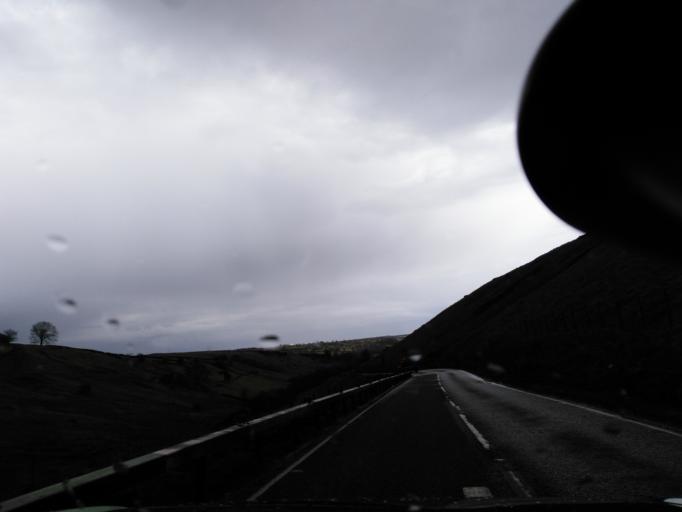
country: GB
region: England
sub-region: Bradford
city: Ilkley
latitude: 53.9935
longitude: -1.7869
